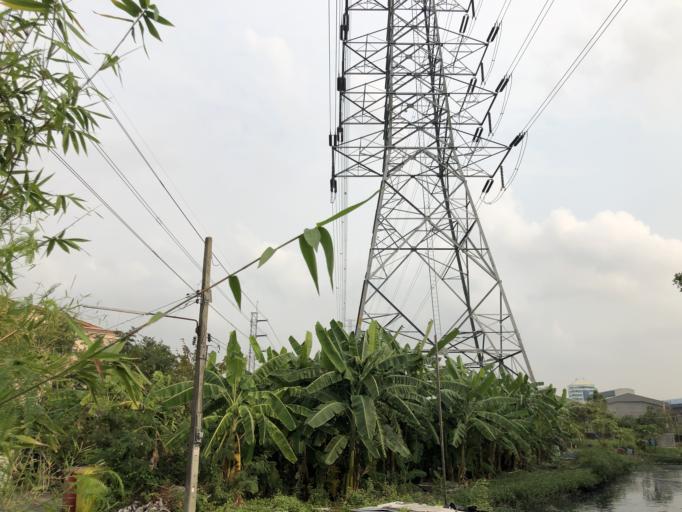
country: TH
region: Bangkok
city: Bang Na
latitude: 13.6034
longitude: 100.6838
